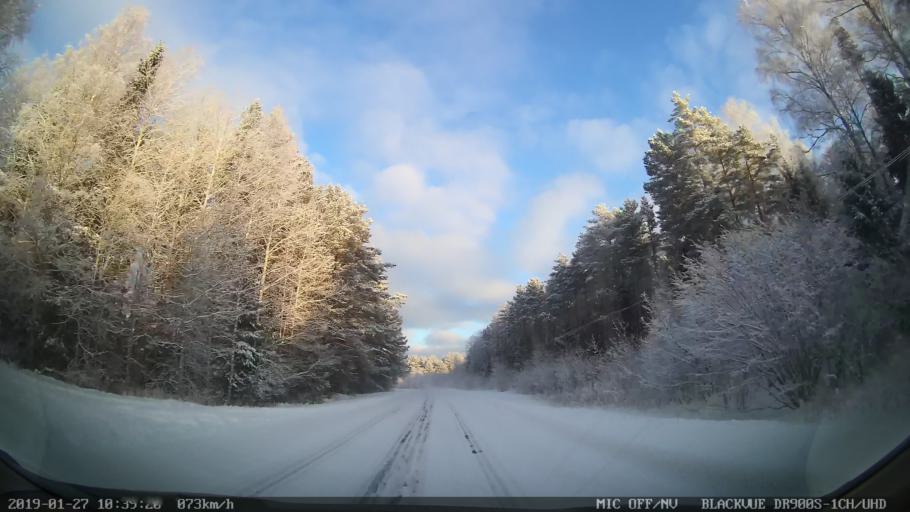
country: EE
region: Harju
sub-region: Raasiku vald
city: Raasiku
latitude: 59.4907
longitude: 25.2621
